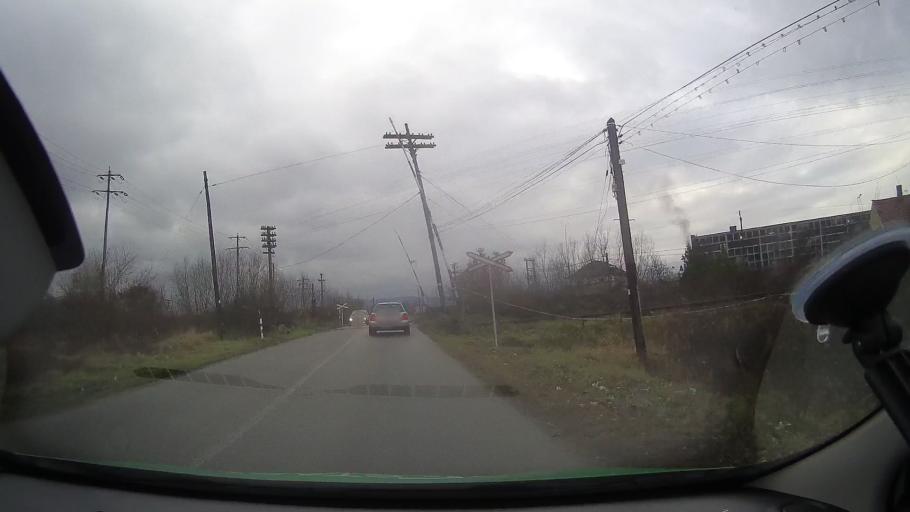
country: RO
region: Arad
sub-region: Comuna Sebis
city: Sebis
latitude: 46.3617
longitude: 22.1307
